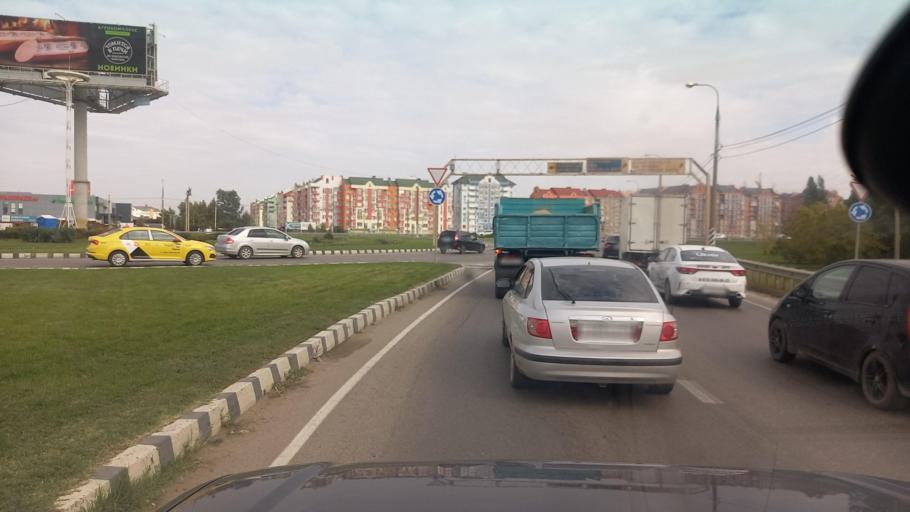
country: RU
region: Krasnodarskiy
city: Krasnodar
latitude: 45.1118
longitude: 38.9241
